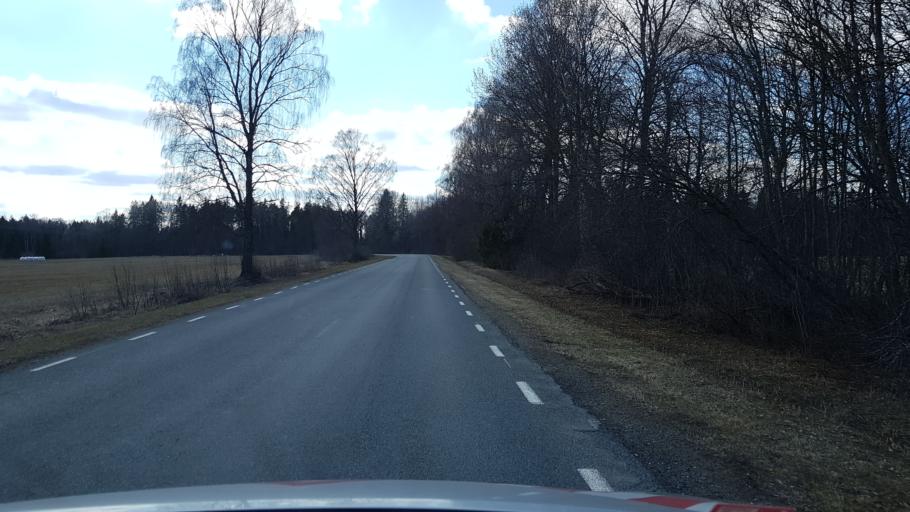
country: EE
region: Laeaene-Virumaa
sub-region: Tapa vald
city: Tapa
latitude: 59.1825
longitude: 26.0140
